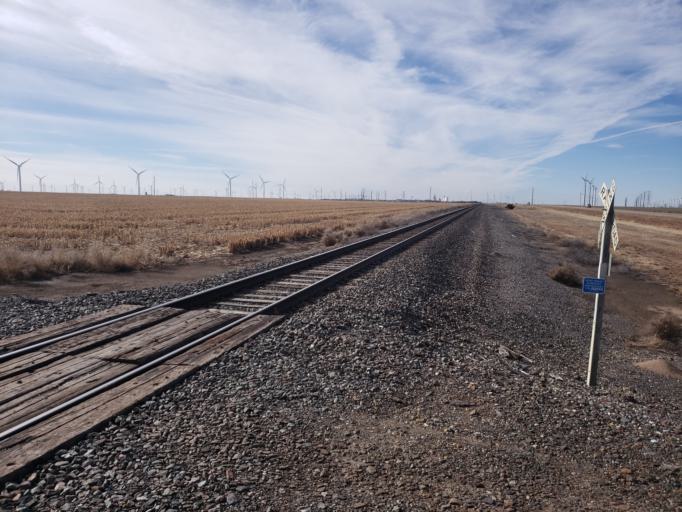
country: US
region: Kansas
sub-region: Hodgeman County
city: Jetmore
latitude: 37.8619
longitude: -99.7167
